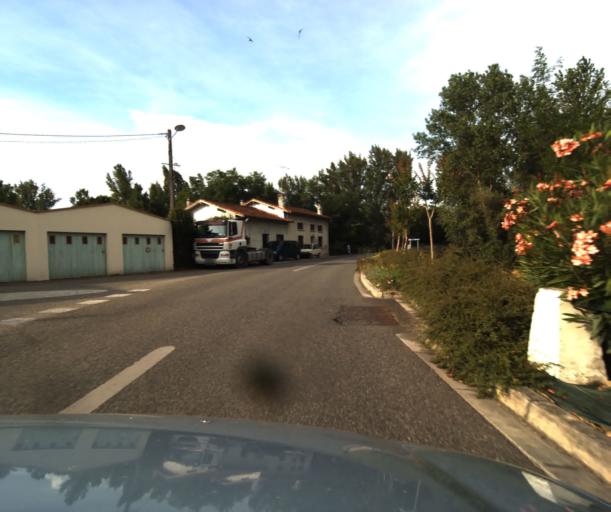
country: FR
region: Midi-Pyrenees
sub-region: Departement du Tarn-et-Garonne
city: Castelsarrasin
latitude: 43.9720
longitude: 1.1203
